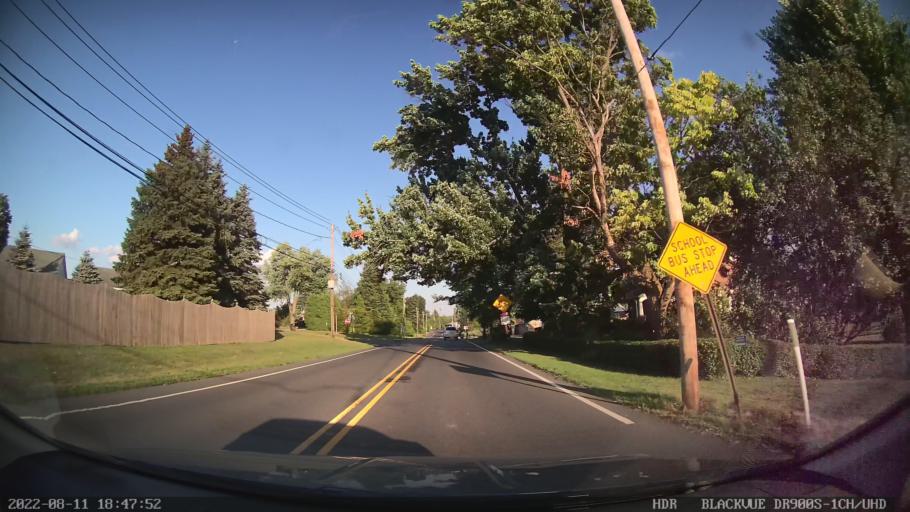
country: US
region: Pennsylvania
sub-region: Lehigh County
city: Wescosville
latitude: 40.5843
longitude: -75.5446
